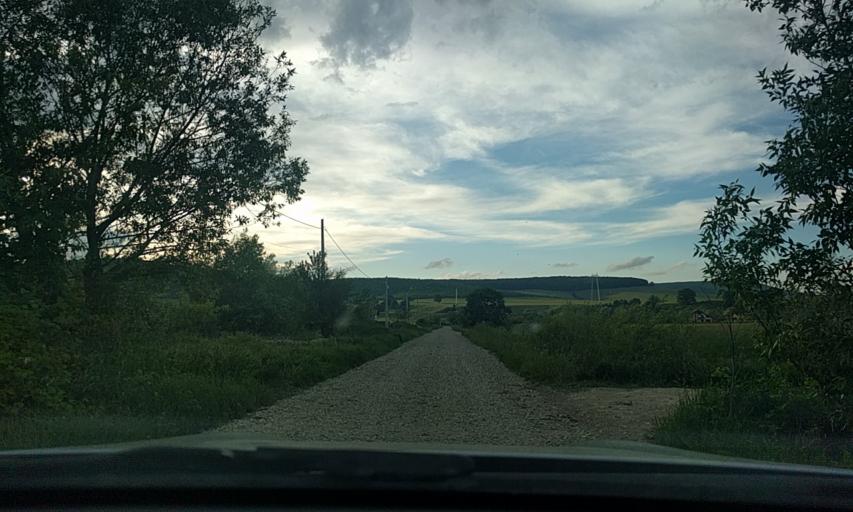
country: RO
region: Covasna
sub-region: Comuna Ilieni
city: Ilieni
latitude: 45.7644
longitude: 25.7193
